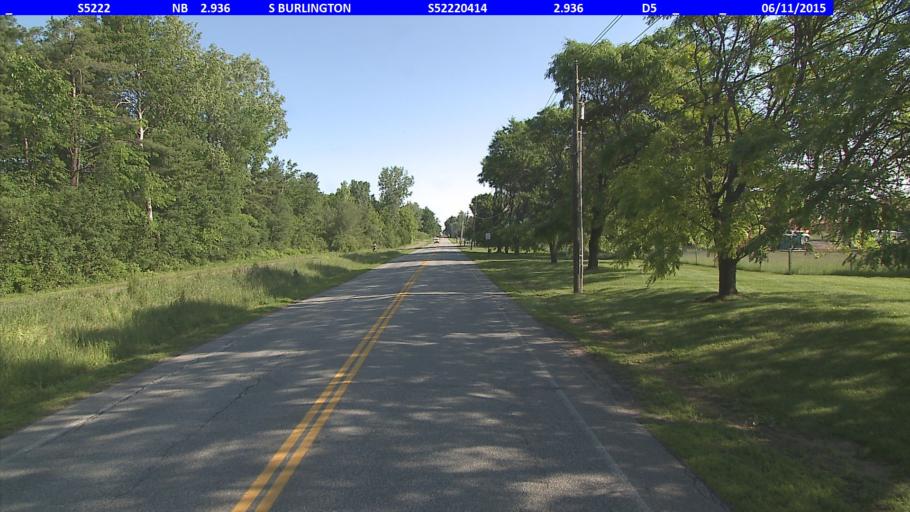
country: US
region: Vermont
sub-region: Chittenden County
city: South Burlington
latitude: 44.4589
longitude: -73.1900
